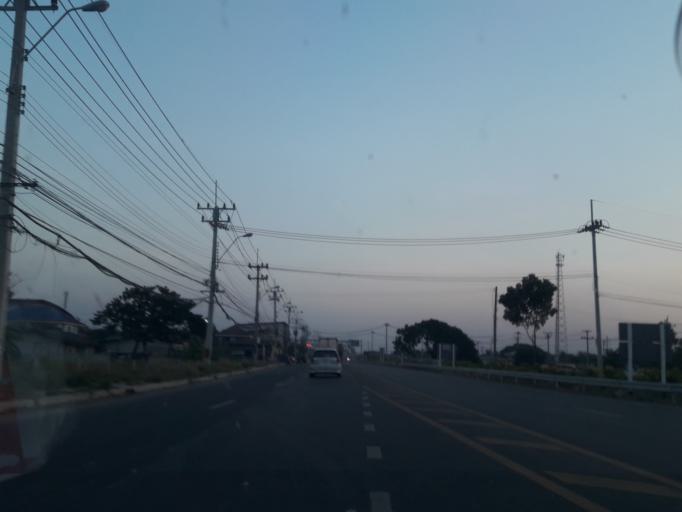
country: TH
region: Pathum Thani
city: Thanyaburi
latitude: 14.0708
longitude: 100.7103
